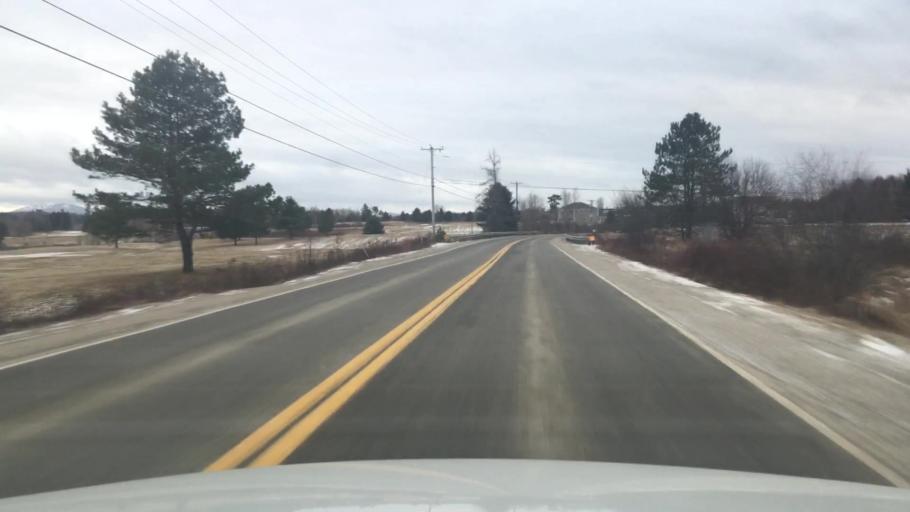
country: US
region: Maine
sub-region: Hancock County
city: Trenton
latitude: 44.4927
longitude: -68.3631
